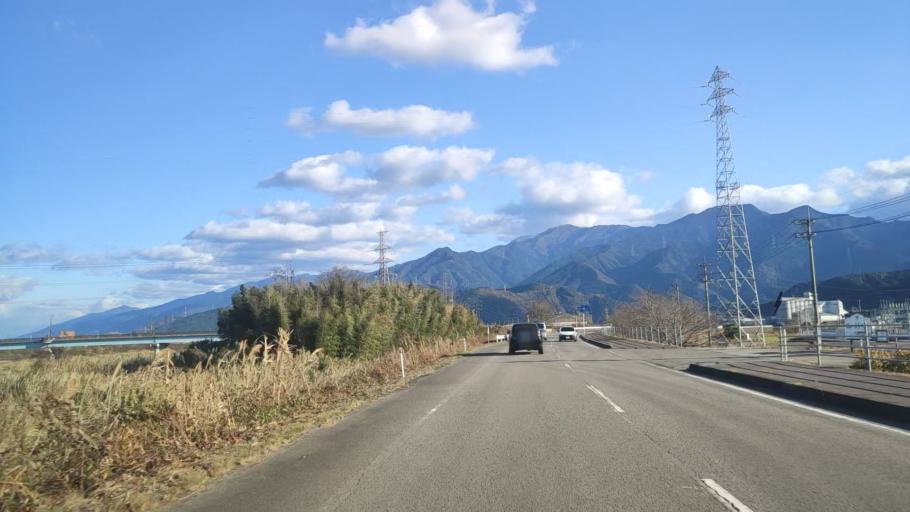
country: JP
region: Ehime
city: Saijo
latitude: 33.9100
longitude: 133.1677
